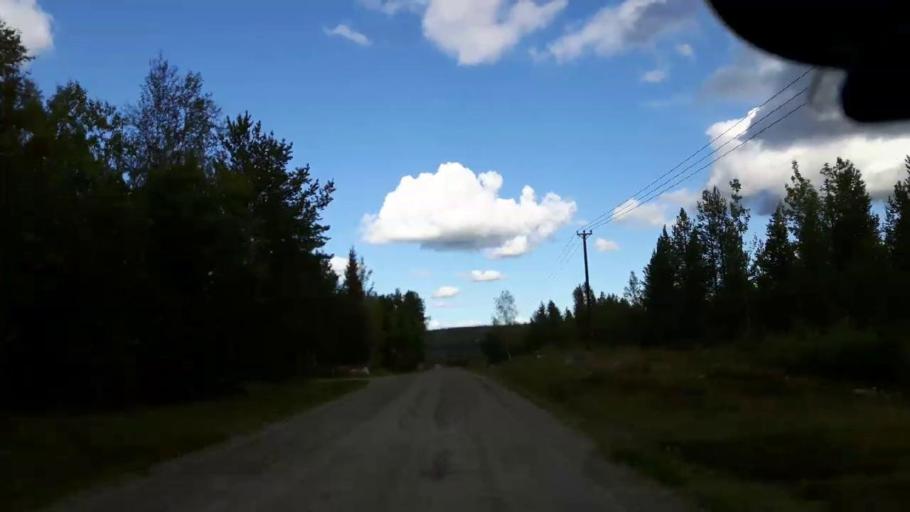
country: SE
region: Jaemtland
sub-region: Stroemsunds Kommun
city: Stroemsund
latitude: 63.4182
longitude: 15.7936
